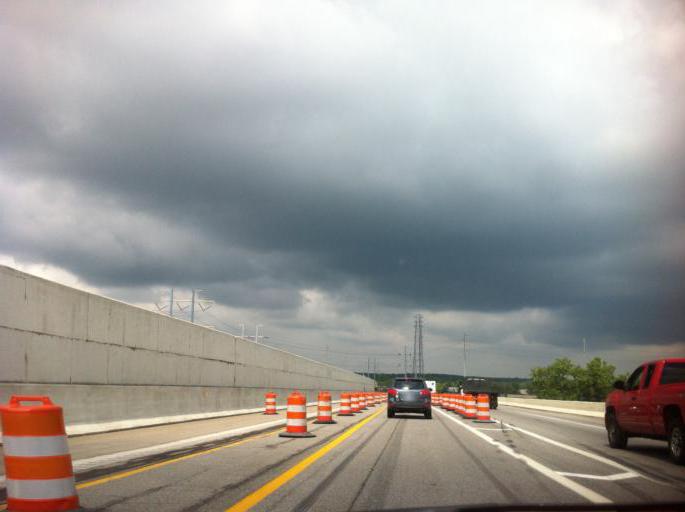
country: US
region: Ohio
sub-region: Cuyahoga County
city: North Royalton
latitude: 41.3109
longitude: -81.7533
